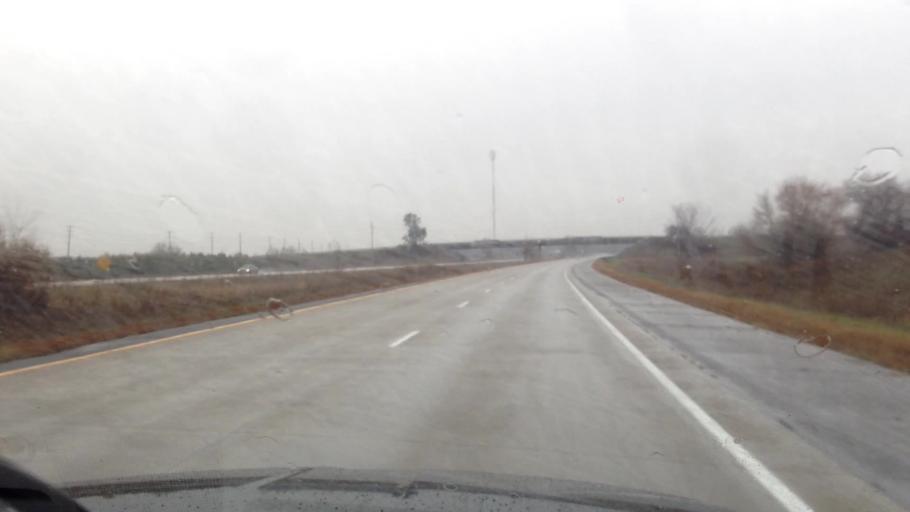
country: CA
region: Ontario
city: Casselman
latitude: 45.3776
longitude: -74.8367
